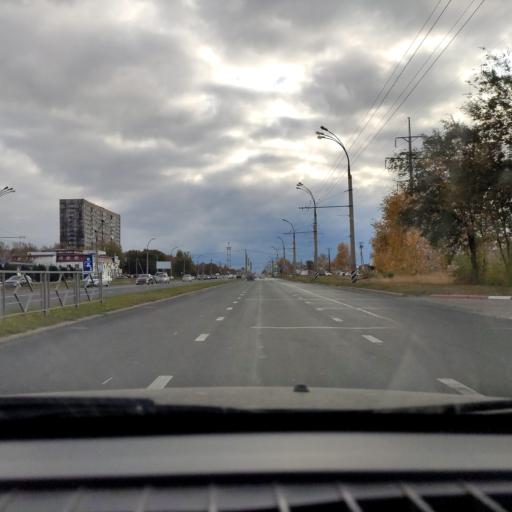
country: RU
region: Samara
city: Tol'yatti
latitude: 53.5418
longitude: 49.2641
